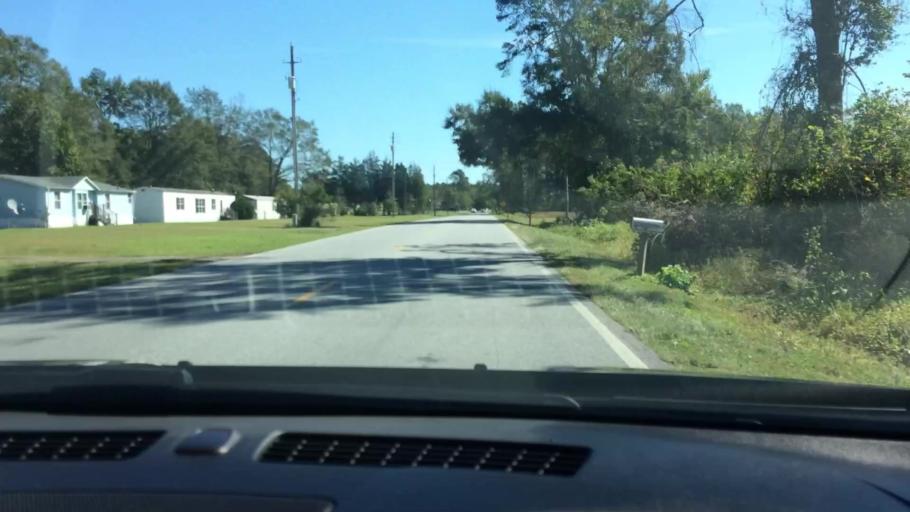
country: US
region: North Carolina
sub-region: Pitt County
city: Grifton
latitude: 35.3765
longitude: -77.3626
